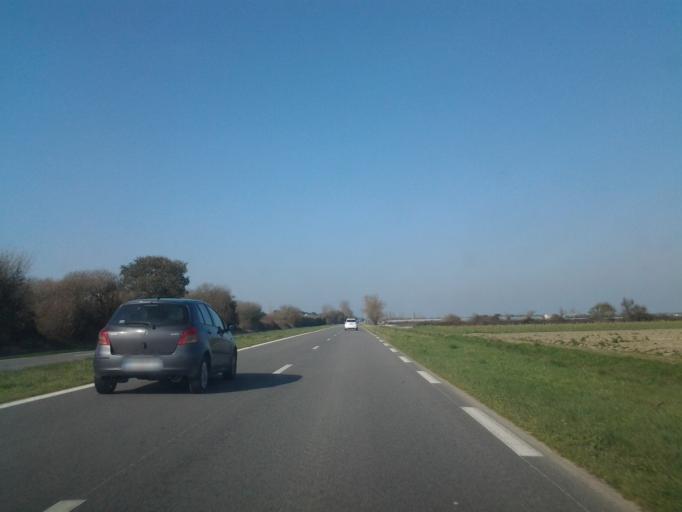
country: FR
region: Pays de la Loire
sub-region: Departement de la Vendee
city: Barbatre
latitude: 46.9578
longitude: -2.1954
